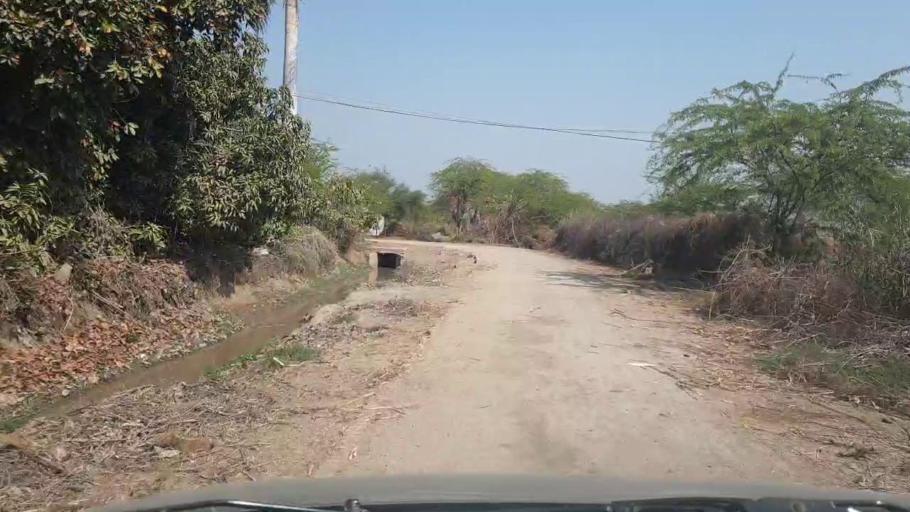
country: PK
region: Sindh
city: Mirwah Gorchani
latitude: 25.2572
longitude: 69.1281
